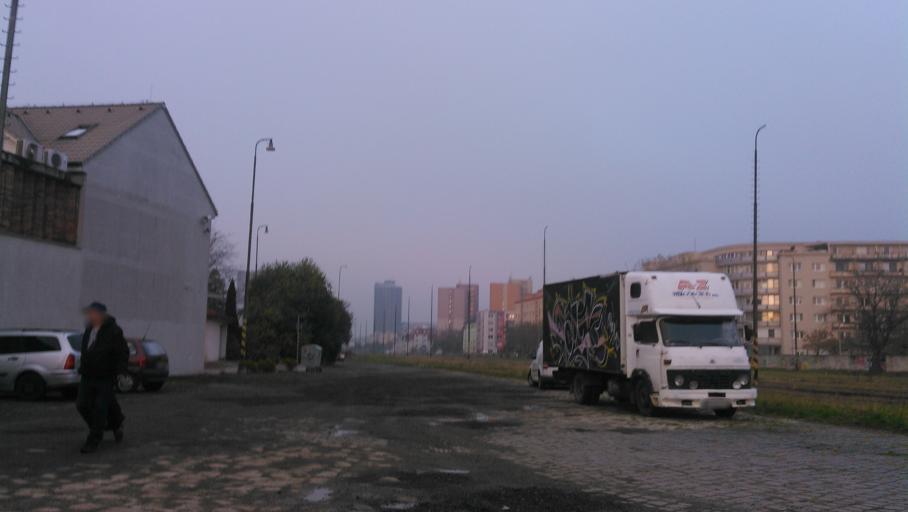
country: SK
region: Bratislavsky
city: Bratislava
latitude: 48.1597
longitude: 17.1256
